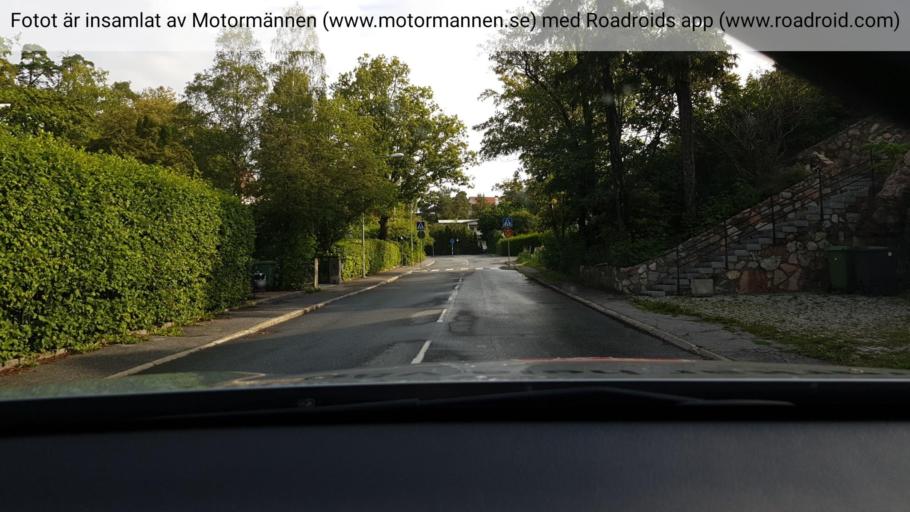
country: SE
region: Stockholm
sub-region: Lidingo
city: Brevik
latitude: 59.3512
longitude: 18.2279
